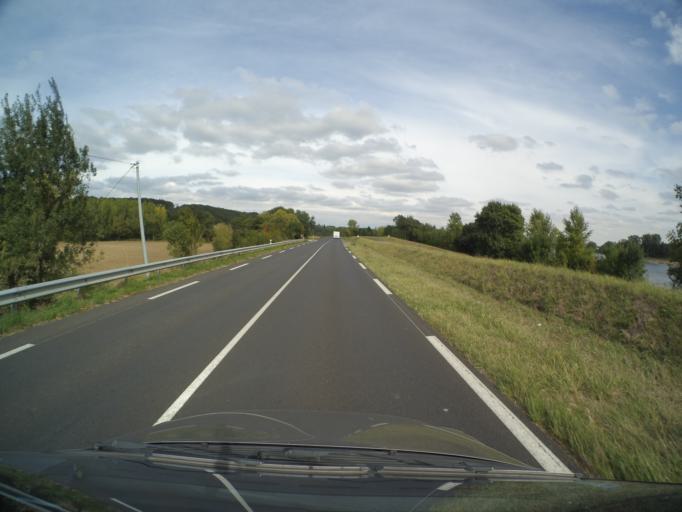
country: FR
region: Centre
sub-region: Departement d'Indre-et-Loire
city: Langeais
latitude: 47.2941
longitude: 0.3364
